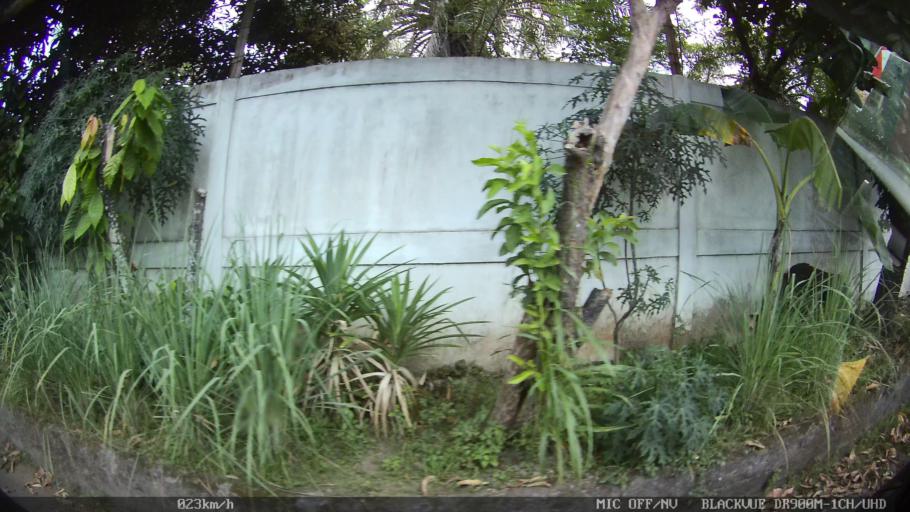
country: ID
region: Daerah Istimewa Yogyakarta
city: Yogyakarta
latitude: -7.8057
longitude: 110.3827
